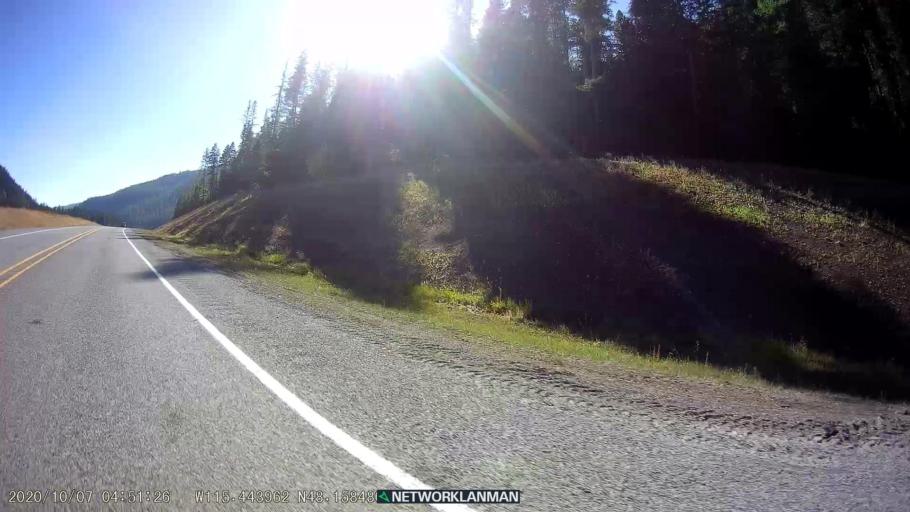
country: US
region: Montana
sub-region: Lincoln County
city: Libby
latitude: 48.1581
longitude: -115.4438
